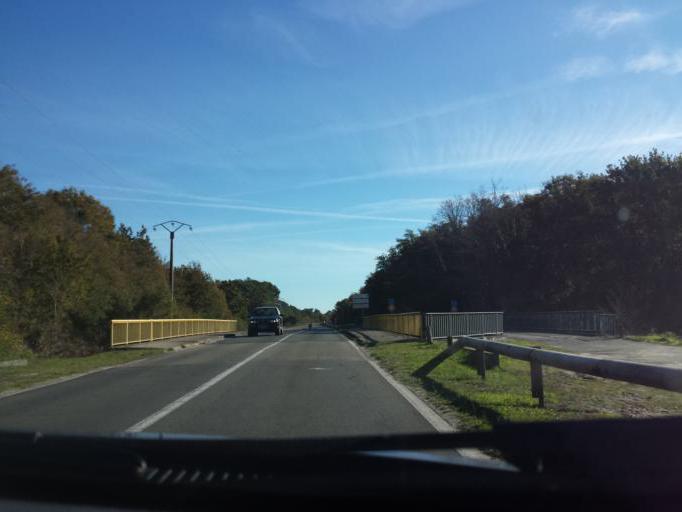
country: FR
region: Aquitaine
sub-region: Departement de la Gironde
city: Lacanau
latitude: 45.0077
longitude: -1.1153
